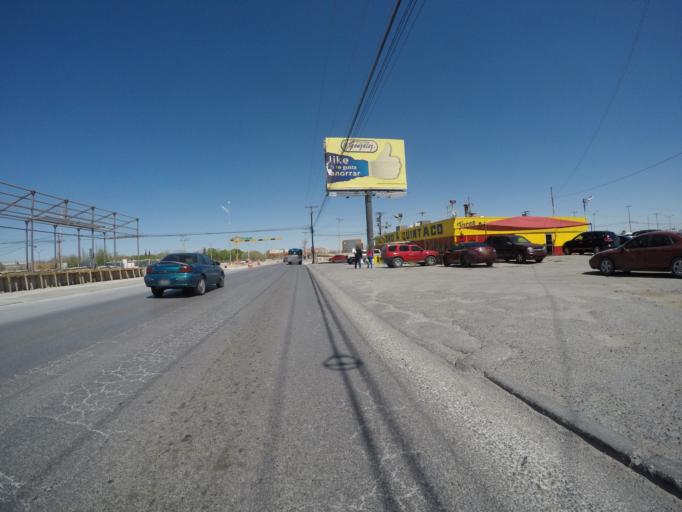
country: MX
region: Chihuahua
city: Ciudad Juarez
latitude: 31.6838
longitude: -106.4244
